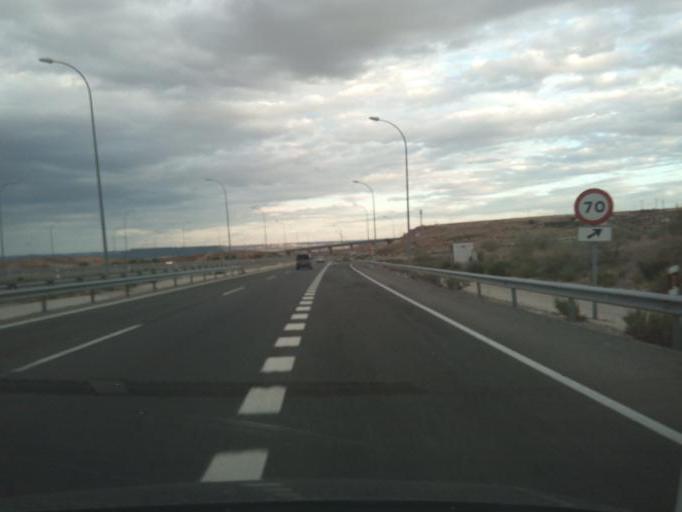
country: ES
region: Madrid
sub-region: Provincia de Madrid
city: Paracuellos de Jarama
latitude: 40.5205
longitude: -3.5059
